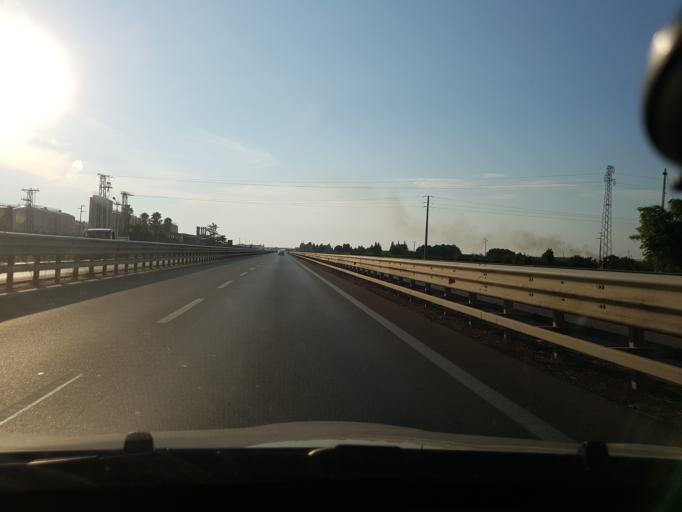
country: IT
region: Apulia
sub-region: Provincia di Foggia
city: Carapelle
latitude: 41.3561
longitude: 15.7171
